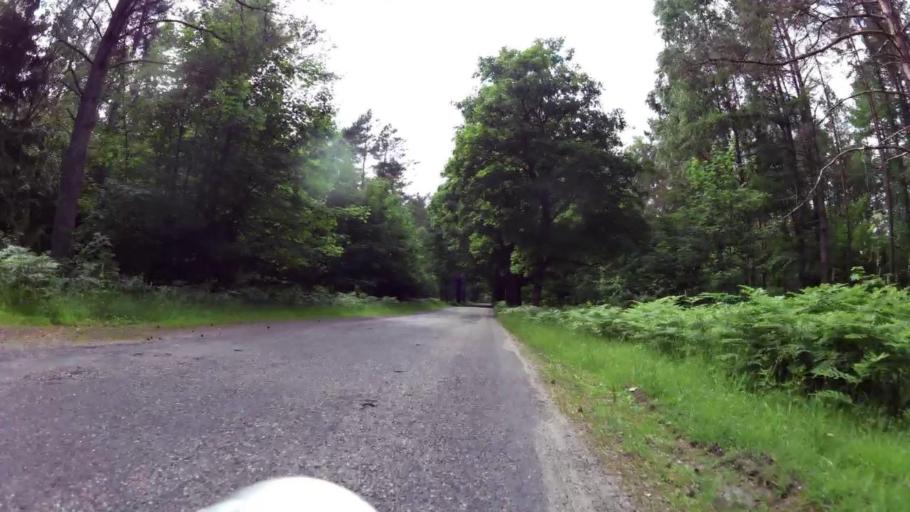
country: PL
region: West Pomeranian Voivodeship
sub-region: Powiat szczecinecki
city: Bialy Bor
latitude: 53.9565
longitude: 16.7477
